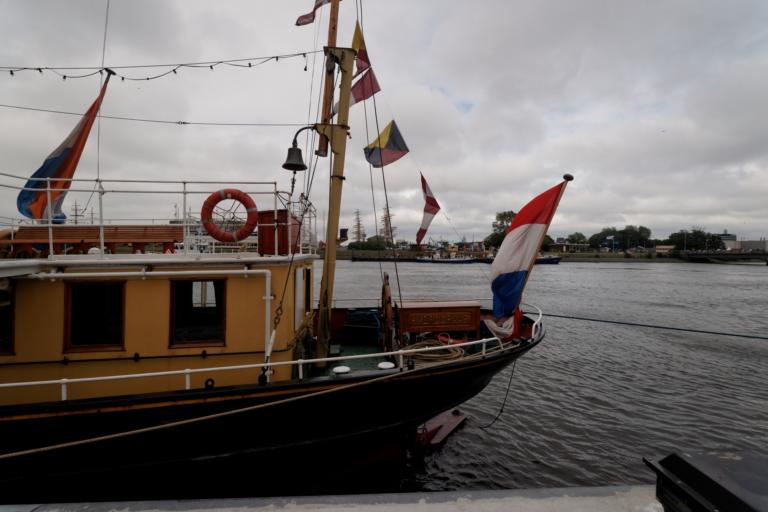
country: NL
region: North Holland
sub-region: Gemeente Den Helder
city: Den Helder
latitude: 52.9558
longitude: 4.7784
